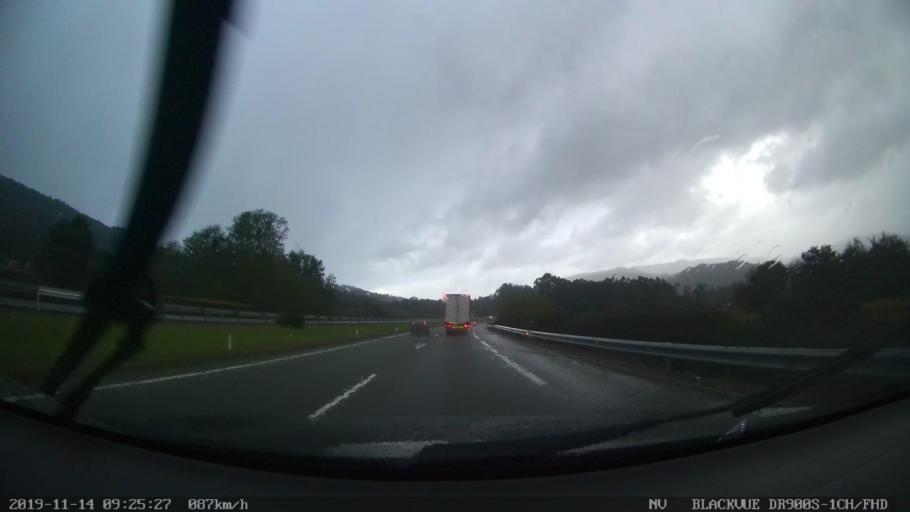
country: ES
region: Galicia
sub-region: Provincia de Pontevedra
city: Marin
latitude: 42.3513
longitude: -8.6467
